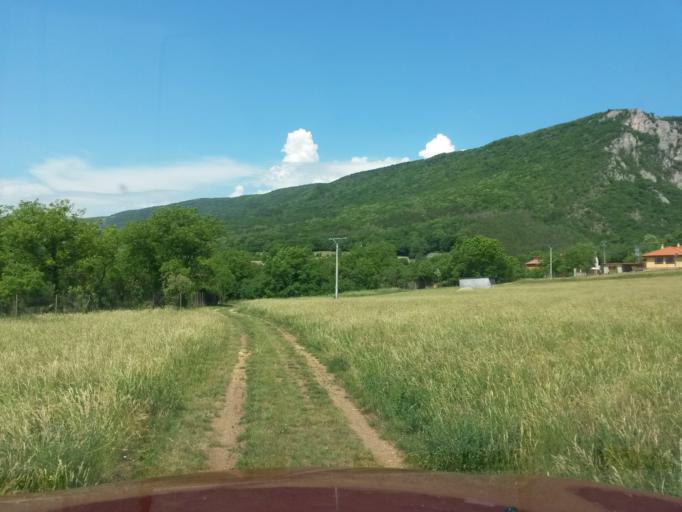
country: SK
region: Kosicky
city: Medzev
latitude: 48.6133
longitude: 20.8360
